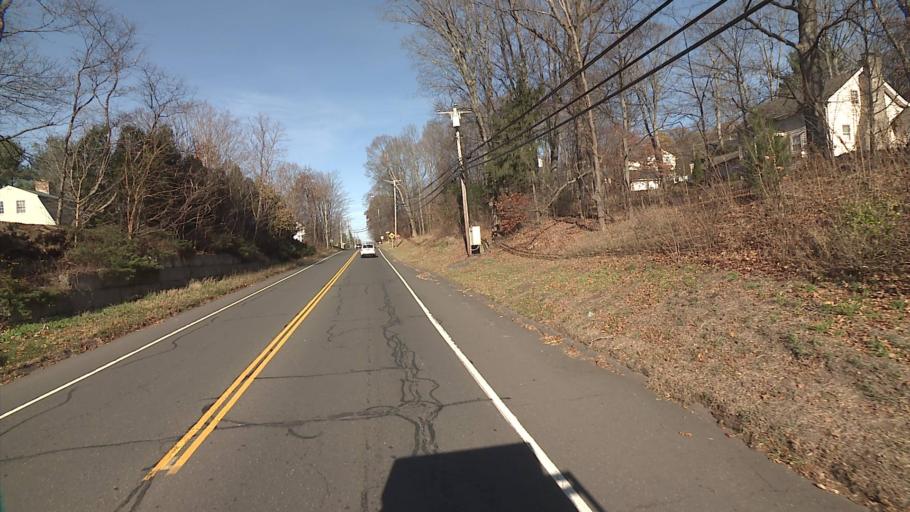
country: US
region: Connecticut
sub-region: Hartford County
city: Glastonbury Center
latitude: 41.6519
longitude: -72.6038
